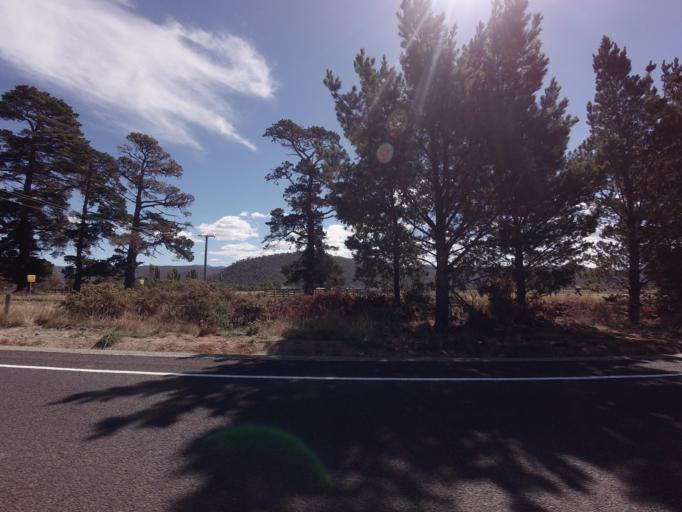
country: AU
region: Tasmania
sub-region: Break O'Day
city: St Helens
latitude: -41.6683
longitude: 147.9046
